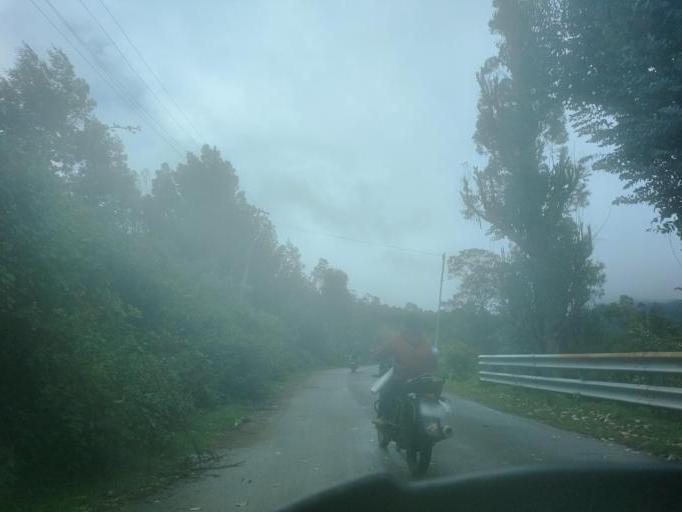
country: IN
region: Tamil Nadu
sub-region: Dindigul
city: Kodaikanal
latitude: 10.2238
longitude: 77.3549
